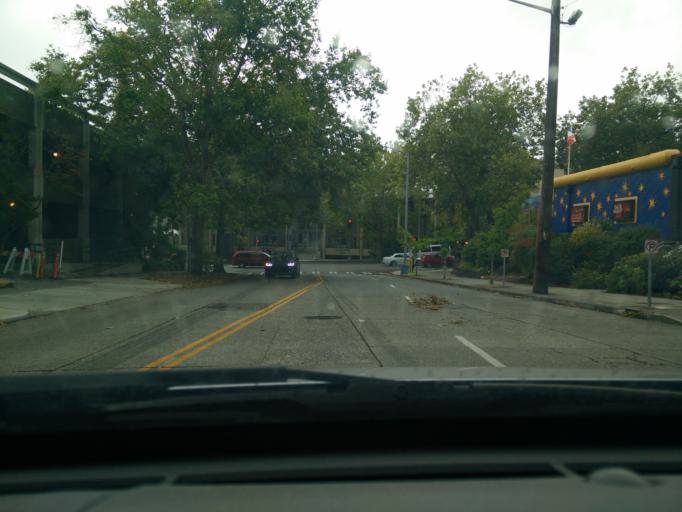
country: US
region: Washington
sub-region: King County
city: Seattle
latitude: 47.6252
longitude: -122.3515
